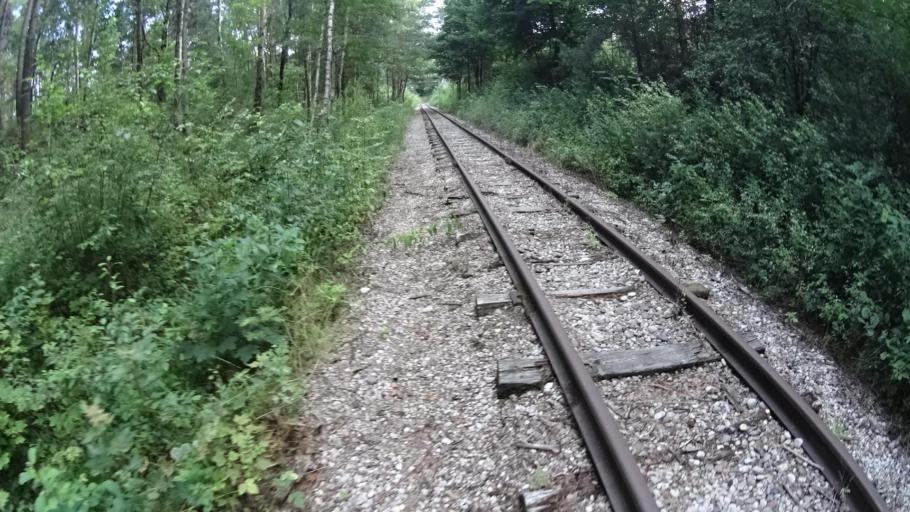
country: PL
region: Masovian Voivodeship
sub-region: Powiat piaseczynski
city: Tarczyn
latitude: 51.9703
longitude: 20.8693
